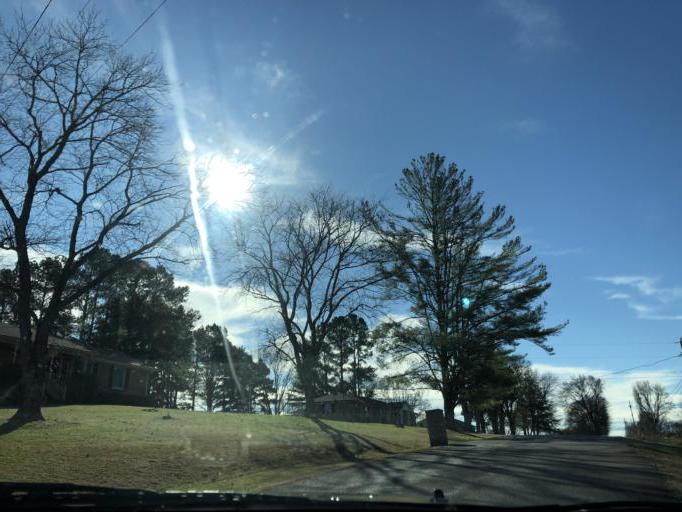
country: US
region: Tennessee
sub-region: Wilson County
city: Mount Juliet
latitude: 36.1790
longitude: -86.5256
